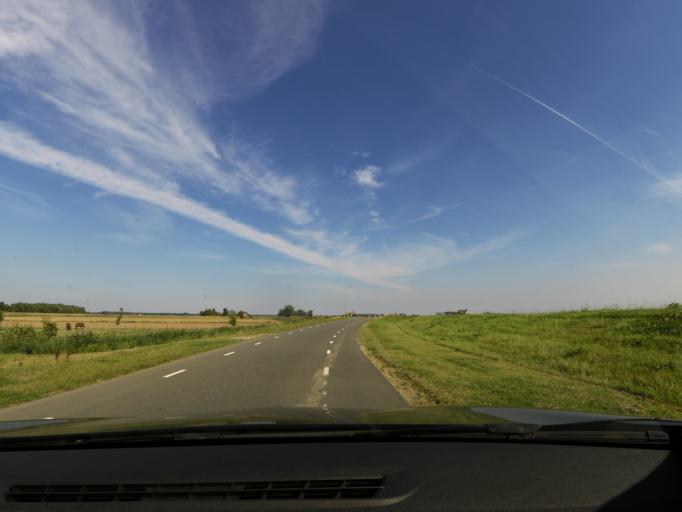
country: NL
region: South Holland
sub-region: Gemeente Hardinxveld-Giessendam
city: Neder-Hardinxveld
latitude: 51.7925
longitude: 4.8240
